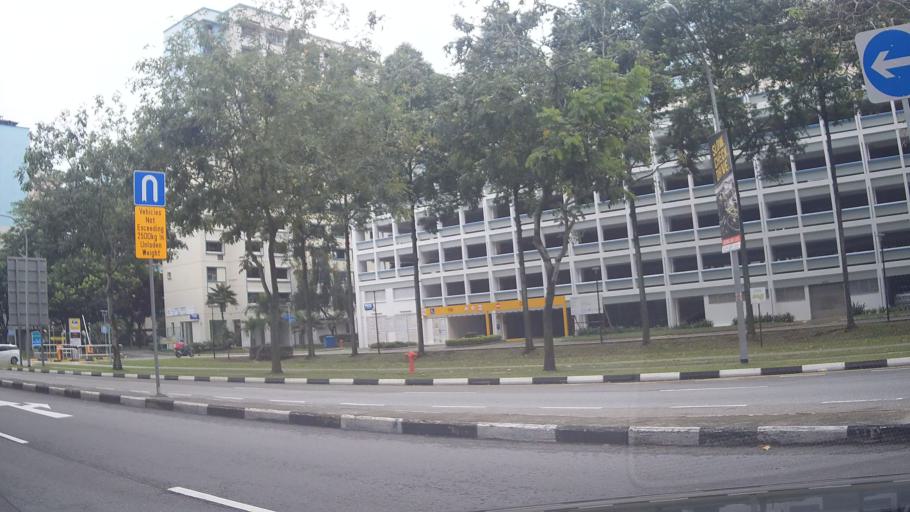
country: MY
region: Johor
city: Johor Bahru
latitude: 1.4423
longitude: 103.8014
